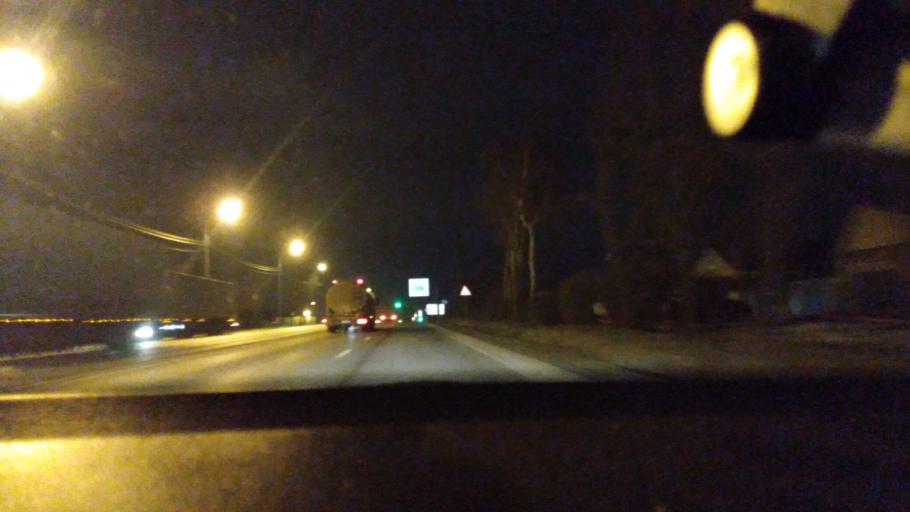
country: RU
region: Moskovskaya
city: Beloozerskiy
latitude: 55.3671
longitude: 38.3968
